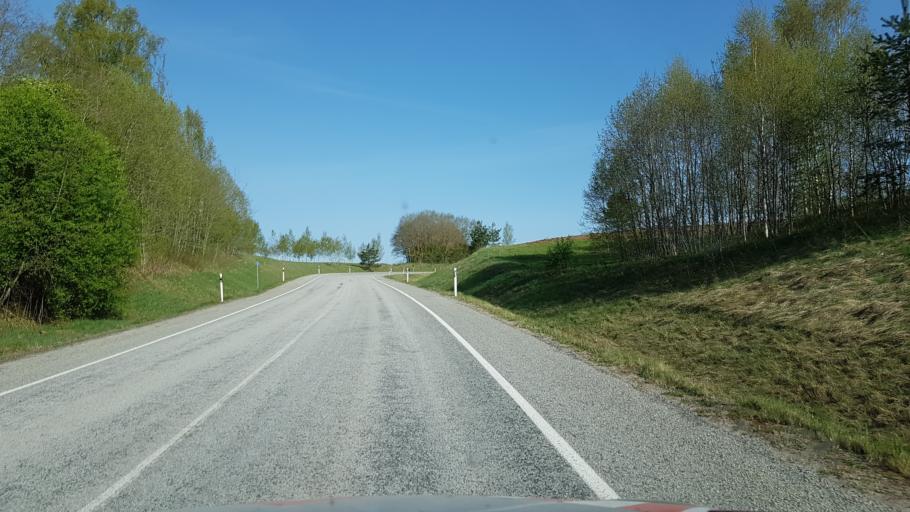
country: EE
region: Viljandimaa
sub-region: Abja vald
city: Abja-Paluoja
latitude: 58.1423
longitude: 25.3761
